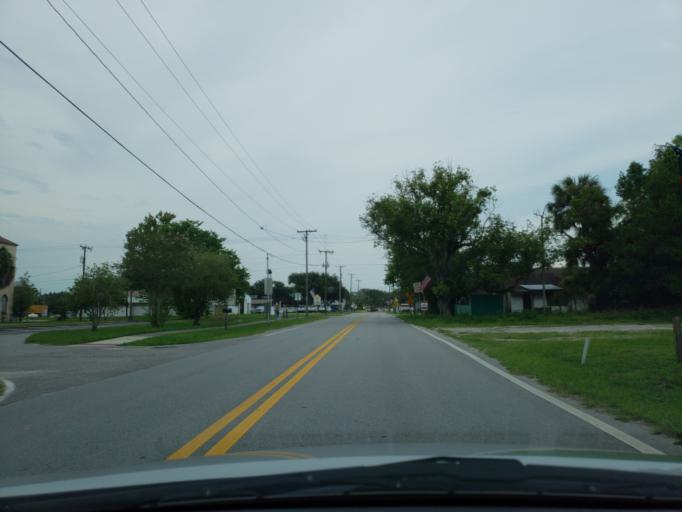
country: US
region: Florida
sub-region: Hillsborough County
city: Lutz
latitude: 28.1510
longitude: -82.4645
